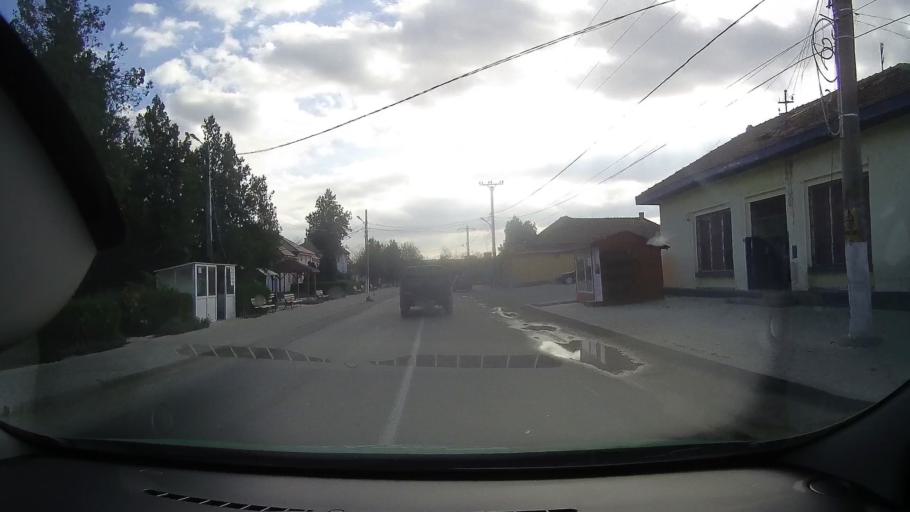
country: RO
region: Constanta
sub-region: Comuna Sacele
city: Sacele
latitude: 44.4870
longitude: 28.6445
